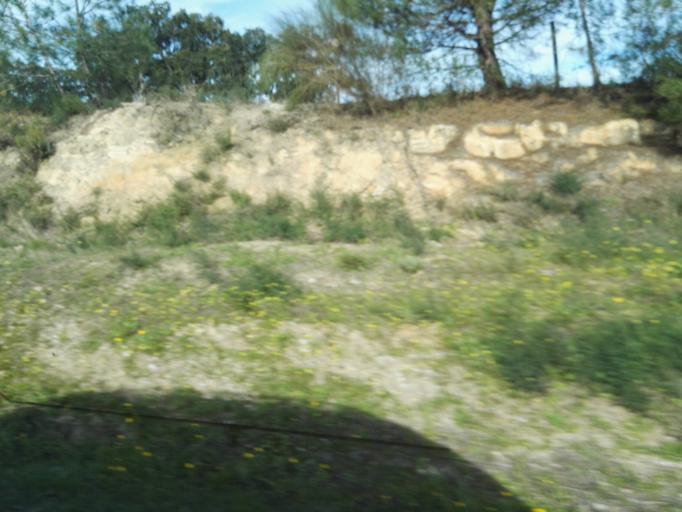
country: PT
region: Evora
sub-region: Mora
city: Mora
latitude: 38.9427
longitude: -8.1331
